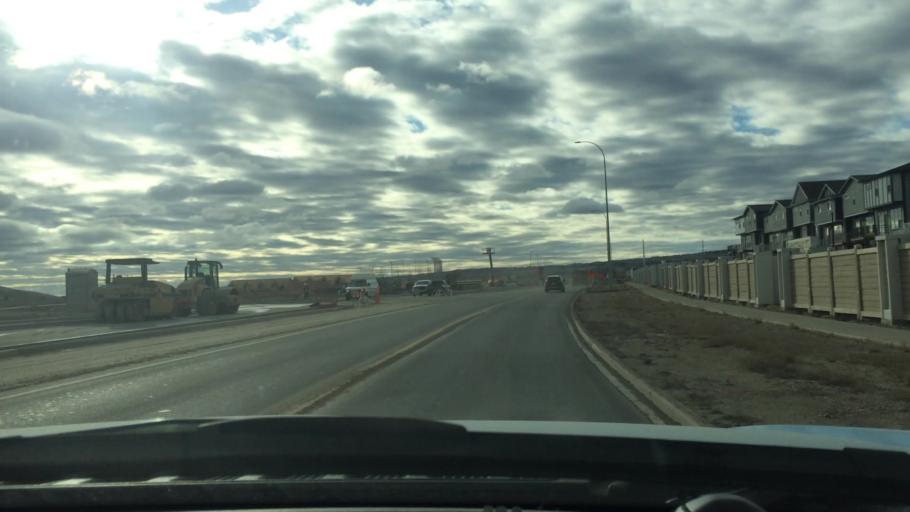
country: CA
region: Alberta
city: Calgary
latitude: 51.1789
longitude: -114.1335
